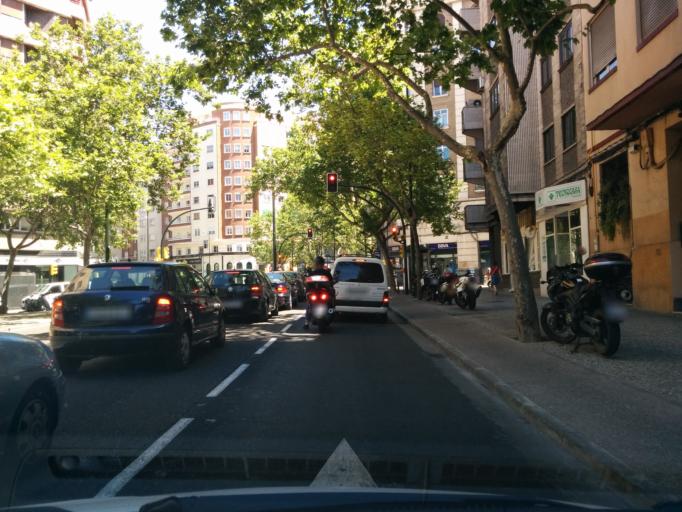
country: ES
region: Aragon
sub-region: Provincia de Zaragoza
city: Zaragoza
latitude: 41.6401
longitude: -0.8875
